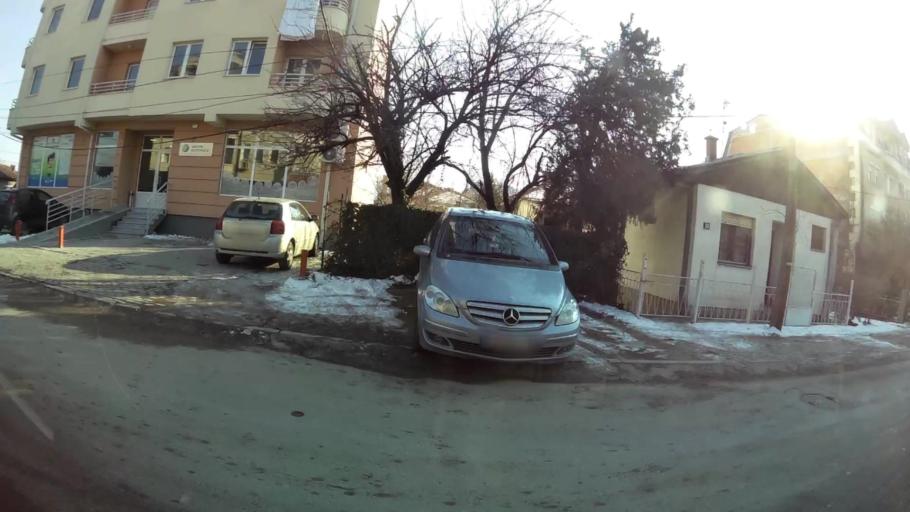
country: MK
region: Karpos
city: Skopje
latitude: 41.9842
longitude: 21.4404
